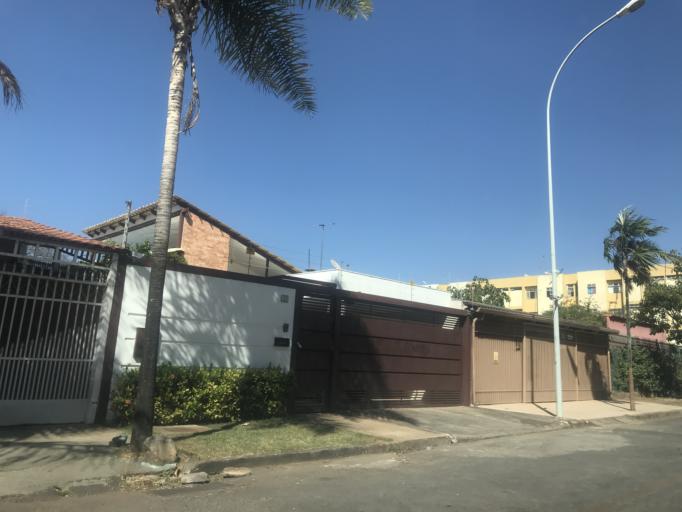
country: BR
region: Federal District
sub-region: Brasilia
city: Brasilia
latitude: -15.8162
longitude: -47.9870
